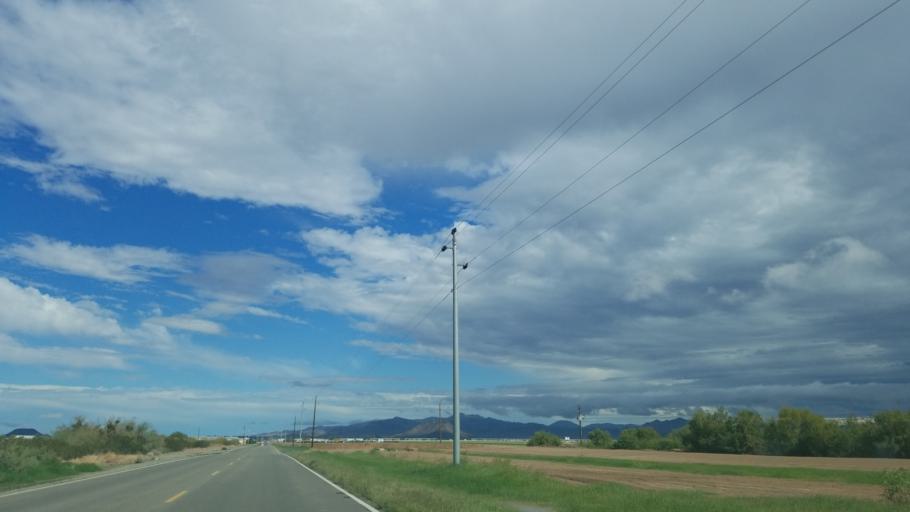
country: US
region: Arizona
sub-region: La Paz County
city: Salome
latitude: 33.6638
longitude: -113.7672
